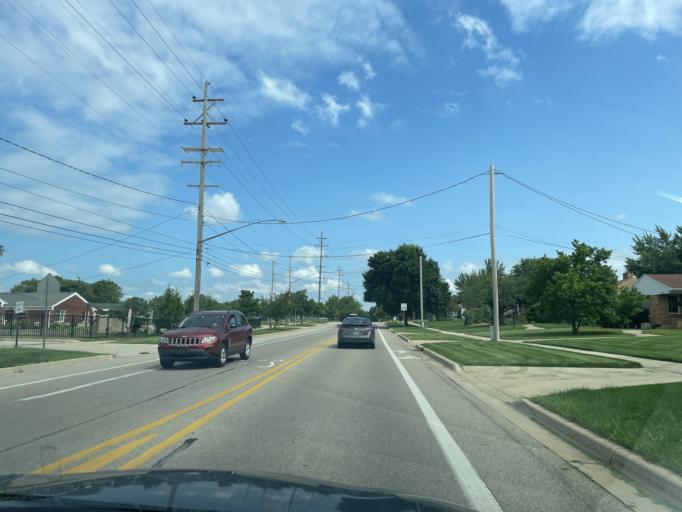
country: US
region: Michigan
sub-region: Kent County
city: East Grand Rapids
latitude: 42.9279
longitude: -85.6239
